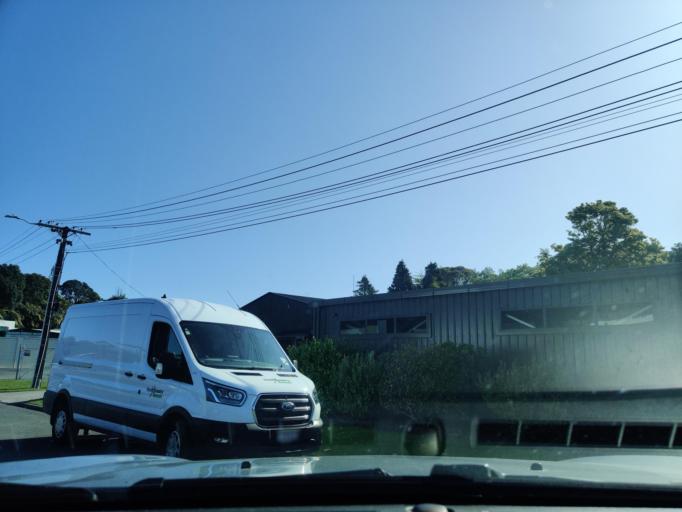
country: NZ
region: Taranaki
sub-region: New Plymouth District
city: New Plymouth
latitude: -39.0771
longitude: 174.0544
